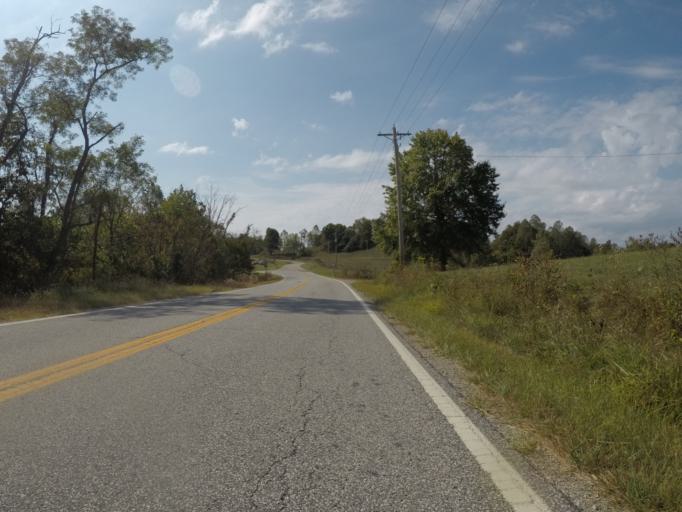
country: US
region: West Virginia
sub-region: Cabell County
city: Lesage
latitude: 38.5874
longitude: -82.4249
